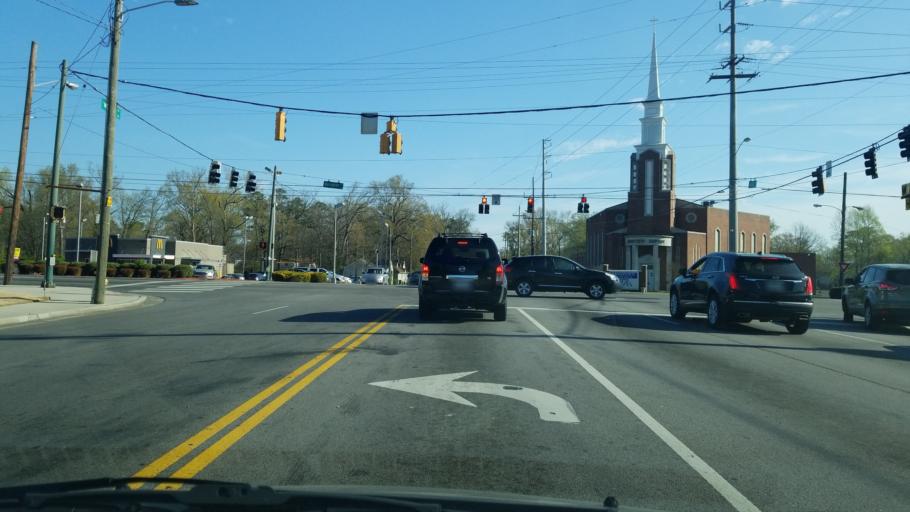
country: US
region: Tennessee
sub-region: Hamilton County
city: East Ridge
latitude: 35.0126
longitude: -85.2284
